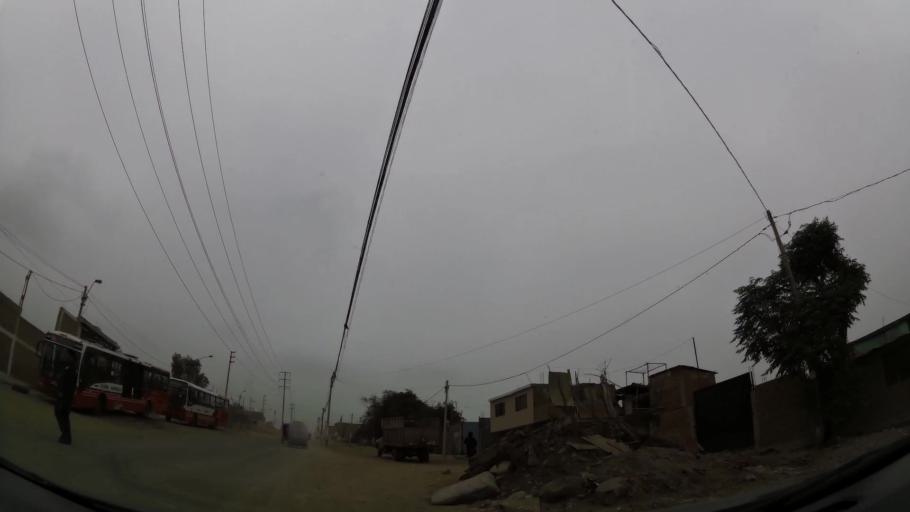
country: PE
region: Lima
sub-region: Lima
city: Surco
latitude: -12.1974
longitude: -76.9693
